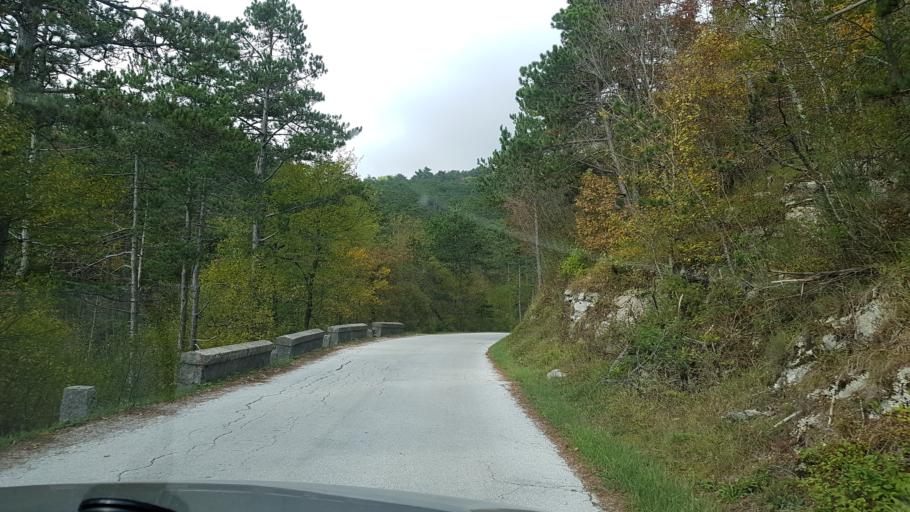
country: HR
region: Istarska
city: Buzet
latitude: 45.4103
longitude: 14.1158
